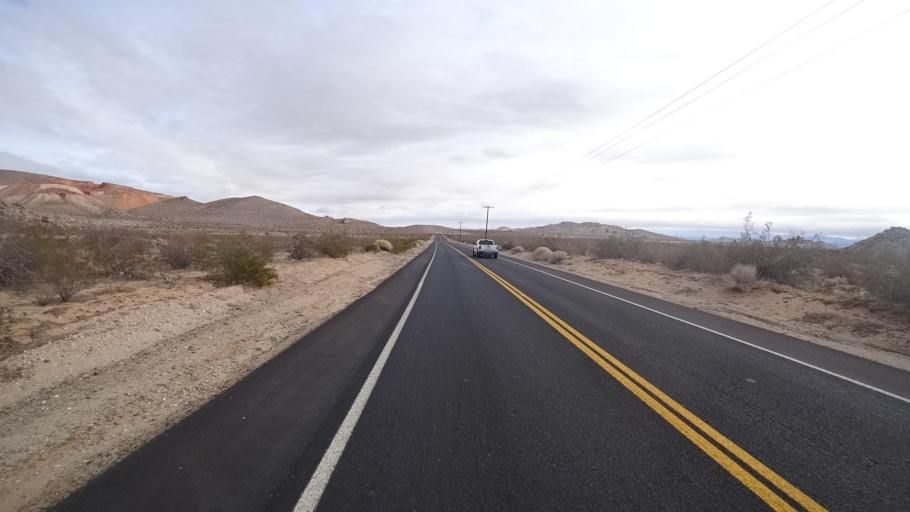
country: US
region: California
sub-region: Kern County
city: Rosamond
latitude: 34.9500
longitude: -118.2850
